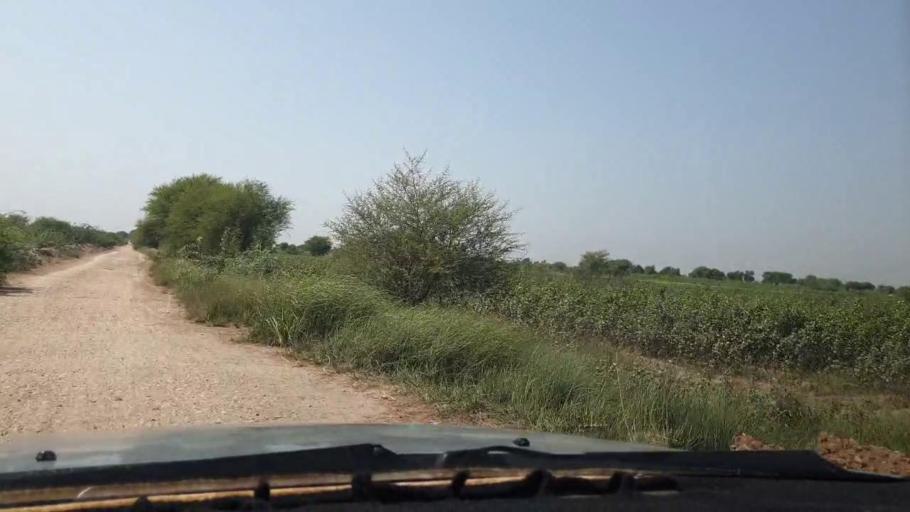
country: PK
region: Sindh
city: Tando Ghulam Ali
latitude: 25.1433
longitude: 68.7943
